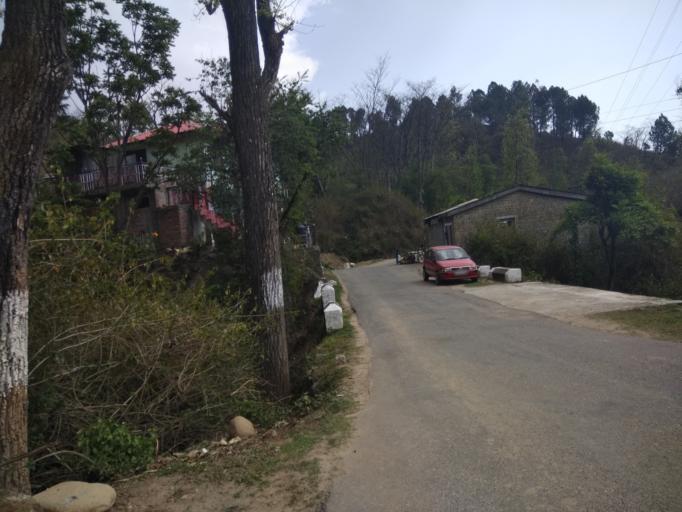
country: IN
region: Himachal Pradesh
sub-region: Kangra
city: Palampur
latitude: 32.0682
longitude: 76.6237
